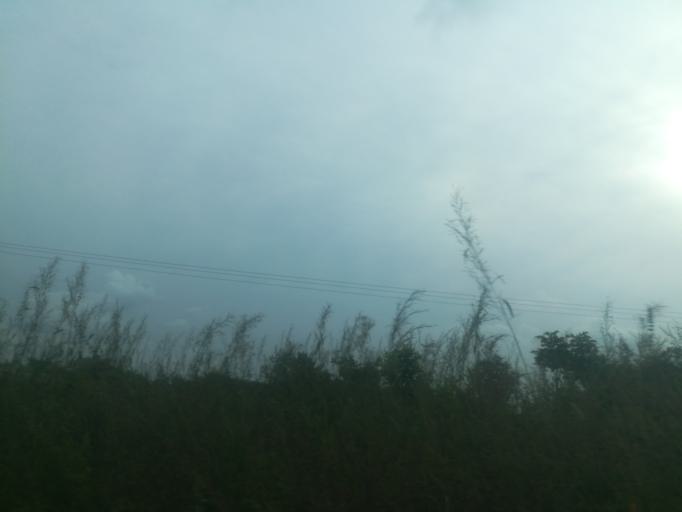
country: NG
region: Ogun
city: Ayetoro
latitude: 7.2358
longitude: 3.1331
